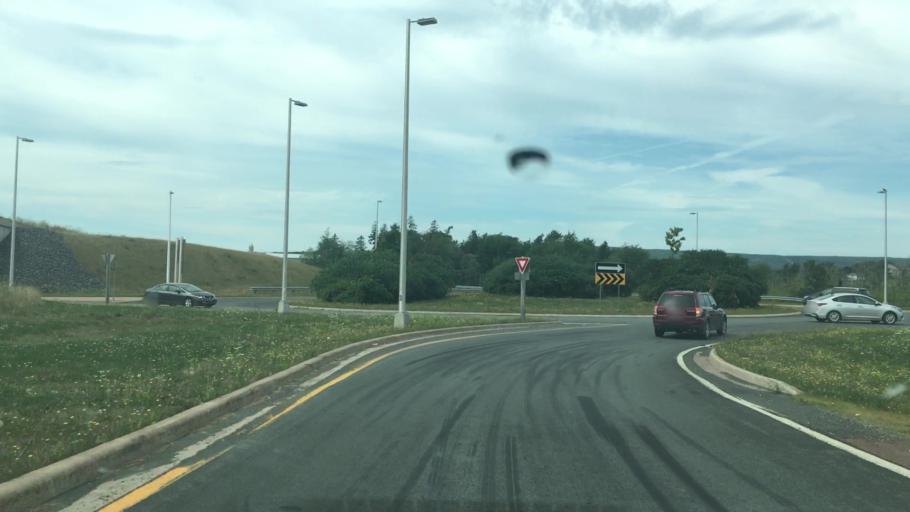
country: CA
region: Nova Scotia
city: Antigonish
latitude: 45.6122
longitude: -61.9984
